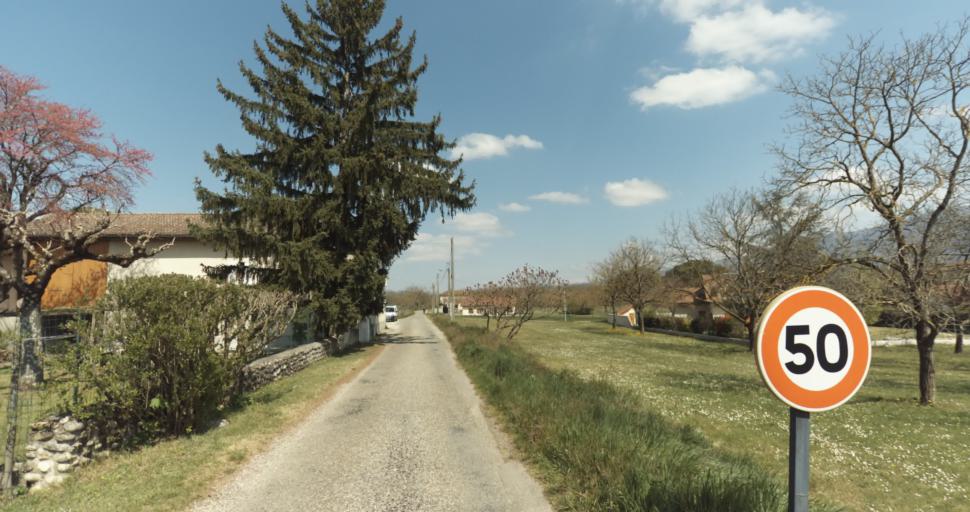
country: FR
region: Rhone-Alpes
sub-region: Departement de l'Isere
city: Saint-Marcellin
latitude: 45.1344
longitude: 5.3150
